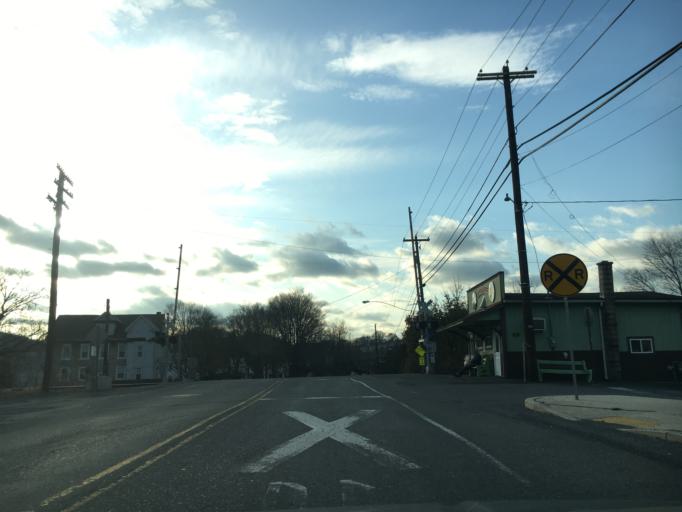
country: US
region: Pennsylvania
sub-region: Carbon County
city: Lehighton
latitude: 40.8303
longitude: -75.6999
